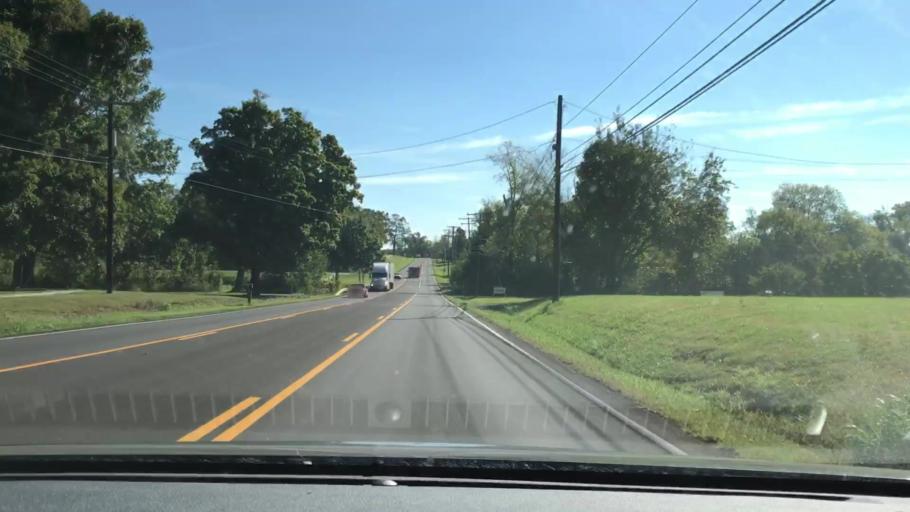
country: US
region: Kentucky
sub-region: Christian County
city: Hopkinsville
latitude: 36.8638
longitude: -87.4548
